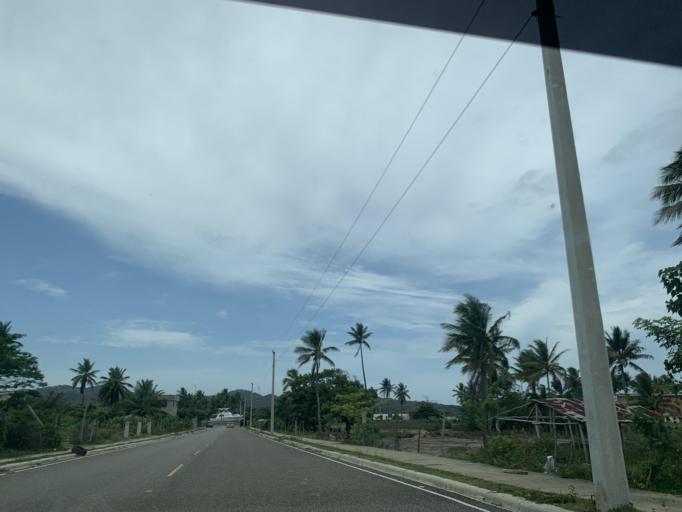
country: DO
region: Puerto Plata
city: Imbert
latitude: 19.8268
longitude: -70.7759
